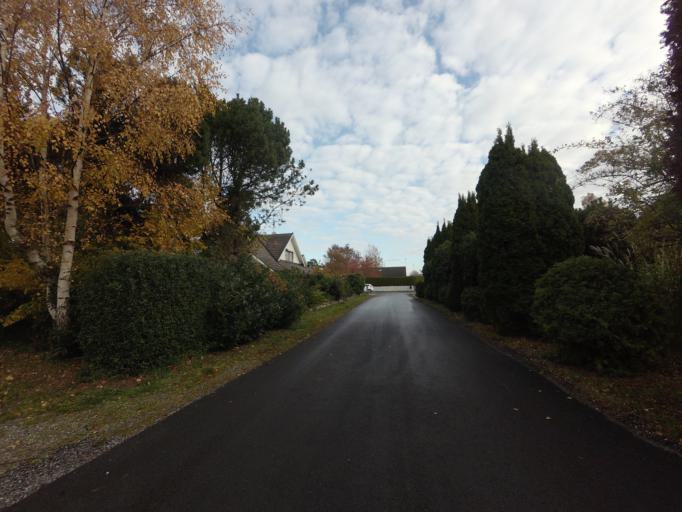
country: SE
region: Skane
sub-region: Vellinge Kommun
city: Hollviken
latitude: 55.4119
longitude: 12.9755
